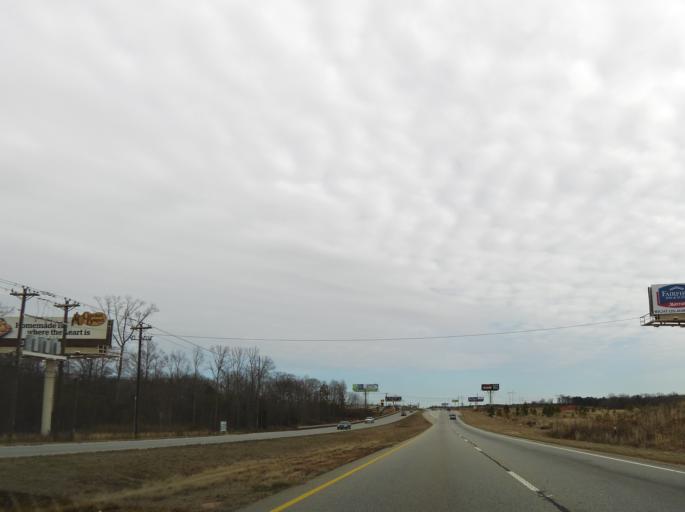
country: US
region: Georgia
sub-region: Houston County
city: Centerville
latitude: 32.6148
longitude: -83.7288
